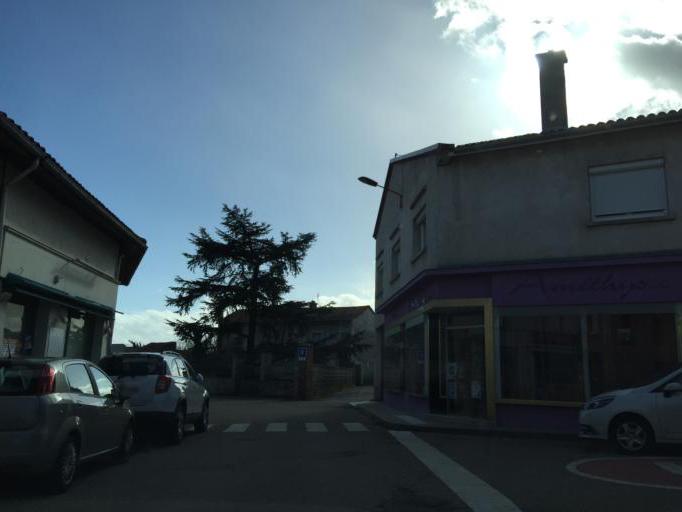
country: FR
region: Rhone-Alpes
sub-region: Departement de la Loire
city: Champdieu
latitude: 45.6464
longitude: 4.0473
